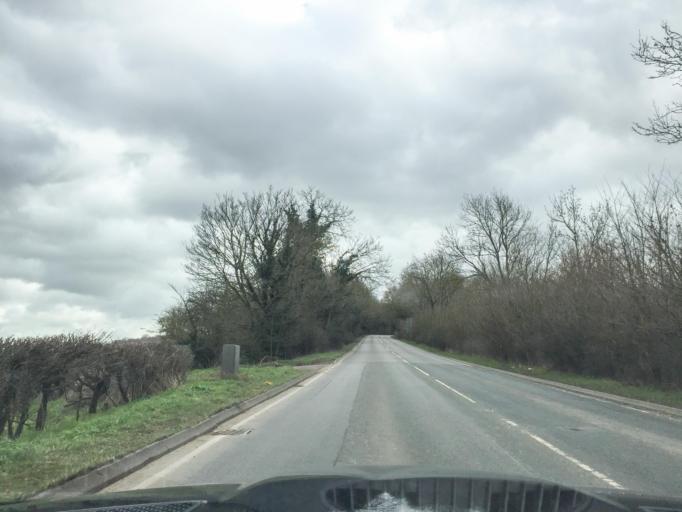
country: GB
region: England
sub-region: Warwickshire
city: Wellesbourne Mountford
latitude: 52.1833
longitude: -1.5976
